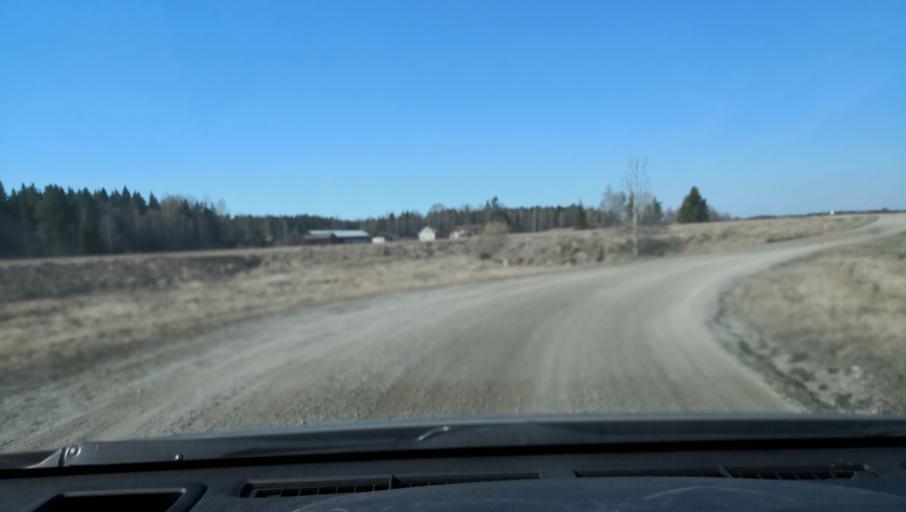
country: SE
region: Vaestmanland
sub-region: Sala Kommun
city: Sala
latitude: 59.8811
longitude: 16.5311
